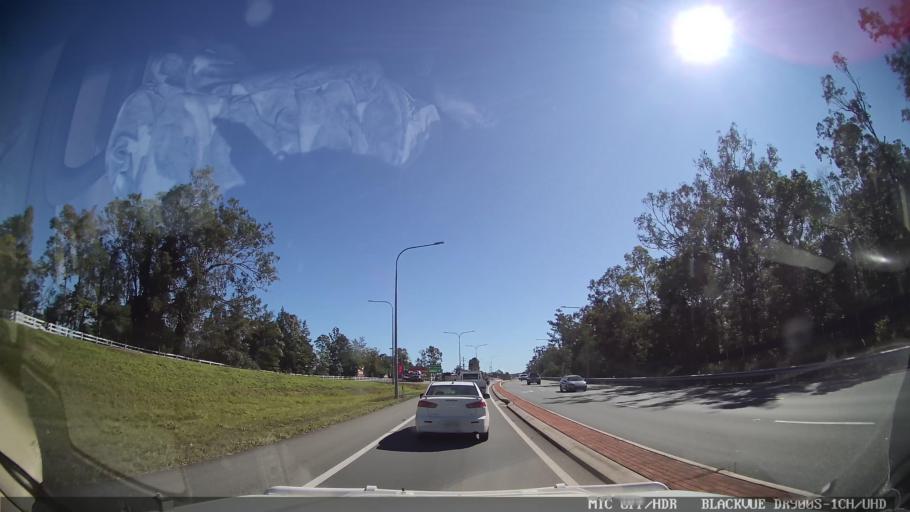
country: AU
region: Queensland
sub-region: Gympie Regional Council
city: Monkland
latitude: -26.2400
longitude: 152.7001
